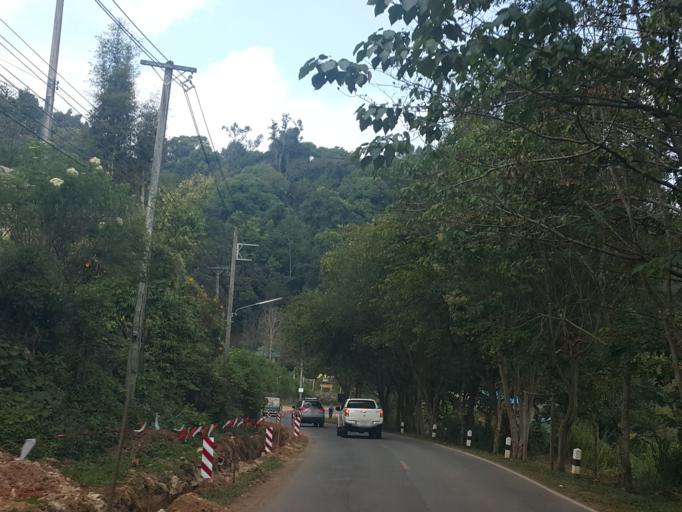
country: TH
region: Chiang Mai
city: Samoeng
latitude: 18.9249
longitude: 98.8224
